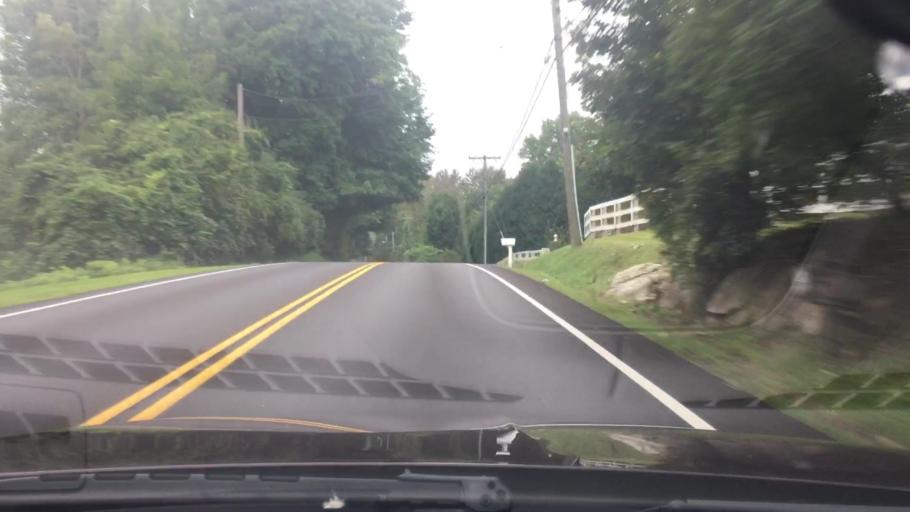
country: US
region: New York
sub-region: Dutchess County
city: Dover Plains
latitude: 41.8556
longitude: -73.5392
